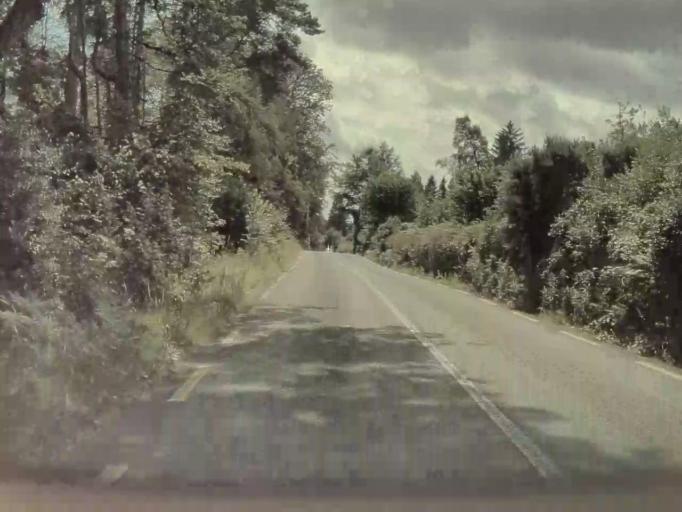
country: IE
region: Leinster
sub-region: Wicklow
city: Rathdrum
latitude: 53.0199
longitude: -6.2744
